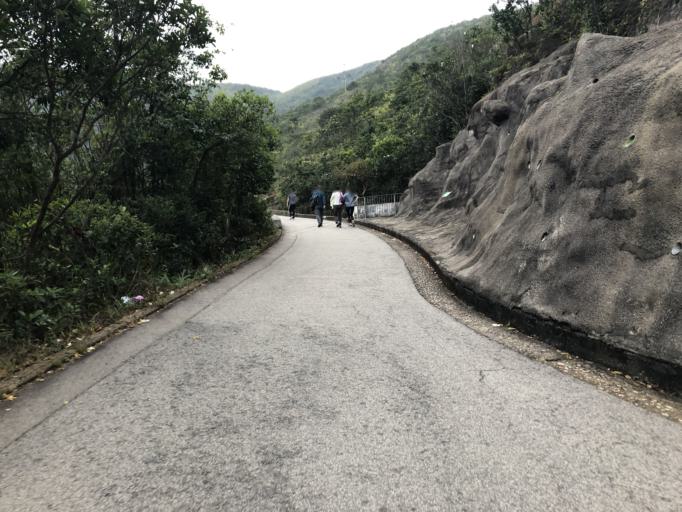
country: HK
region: Wanchai
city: Wan Chai
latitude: 22.2730
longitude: 114.2105
